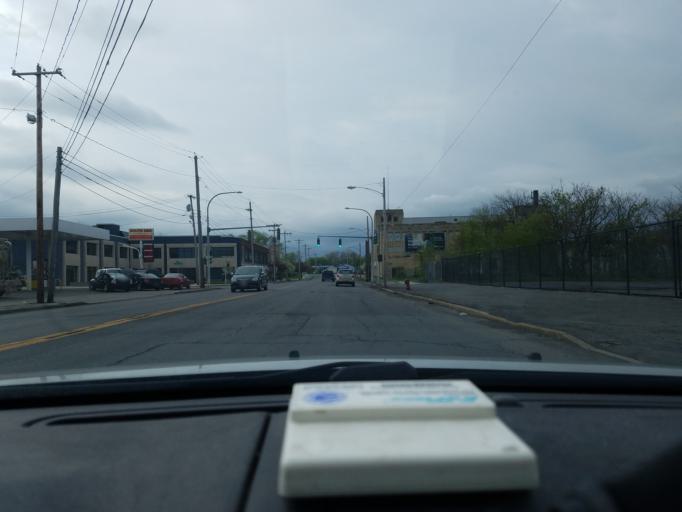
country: US
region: New York
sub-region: Onondaga County
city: Syracuse
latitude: 43.0359
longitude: -76.1496
